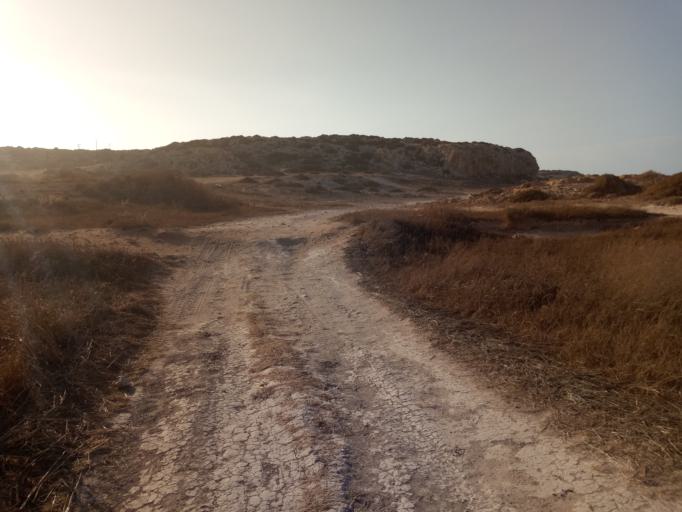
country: CY
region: Ammochostos
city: Protaras
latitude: 34.9675
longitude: 34.0762
